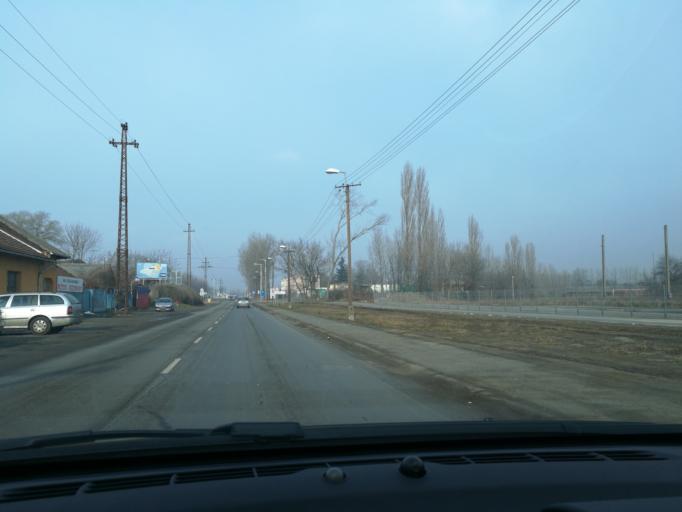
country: HU
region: Szabolcs-Szatmar-Bereg
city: Nyiregyhaza
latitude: 47.9646
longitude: 21.6992
